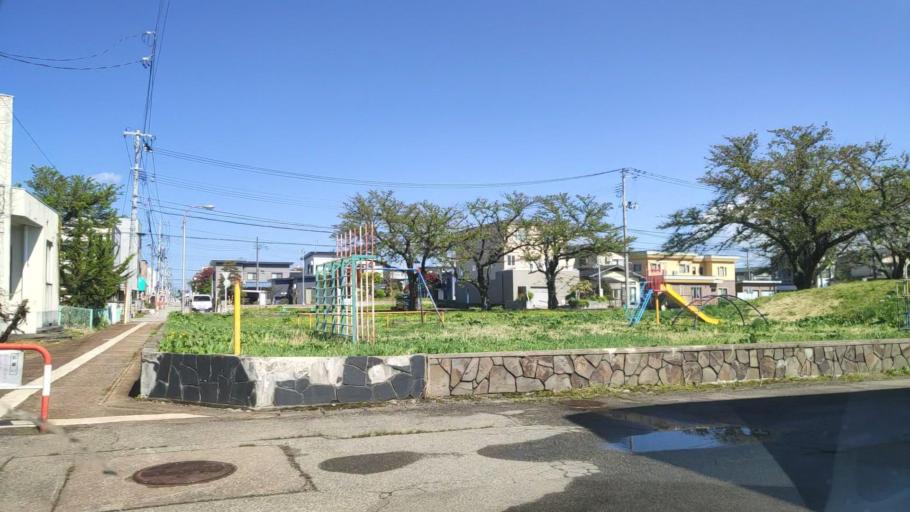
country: JP
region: Akita
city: Omagari
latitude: 39.4667
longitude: 140.4748
